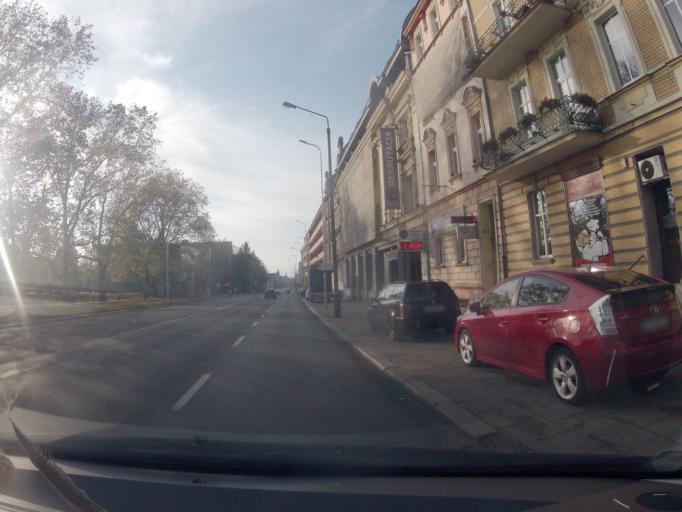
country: PL
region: Opole Voivodeship
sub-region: Powiat opolski
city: Opole
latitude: 50.6681
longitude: 17.9399
